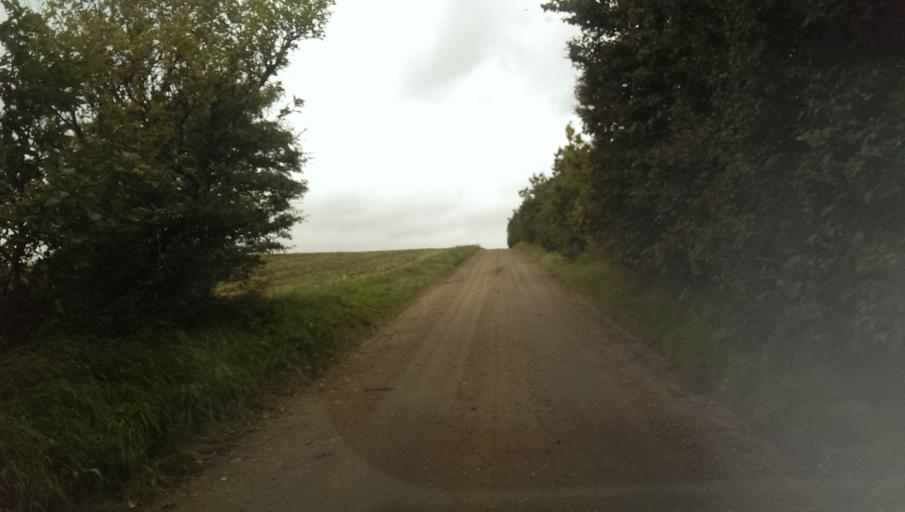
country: DK
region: South Denmark
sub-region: Esbjerg Kommune
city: Tjaereborg
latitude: 55.4821
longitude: 8.6004
